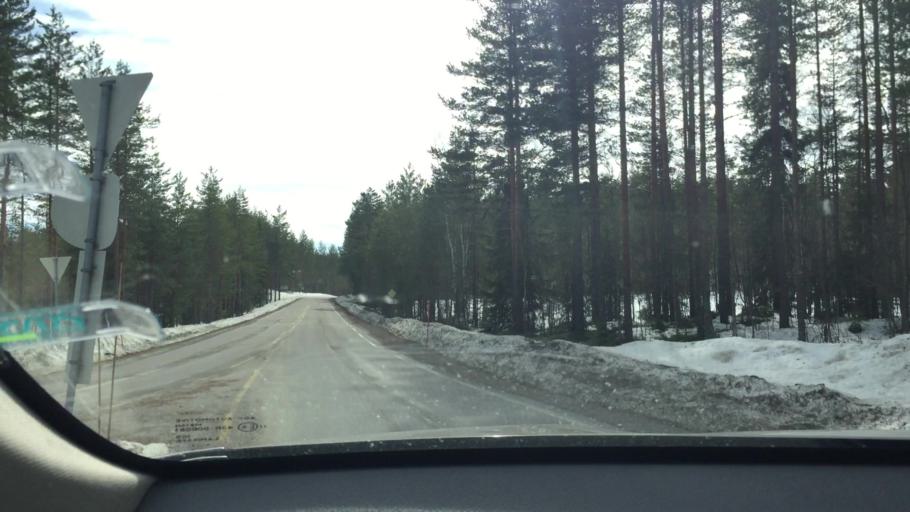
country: NO
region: Hedmark
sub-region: Trysil
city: Innbygda
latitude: 61.0755
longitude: 12.5744
